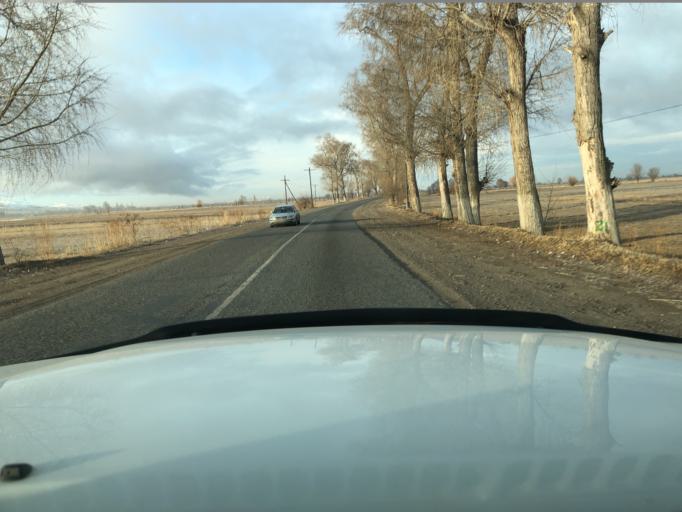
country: KG
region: Ysyk-Koel
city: Karakol
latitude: 42.4756
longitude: 78.3179
